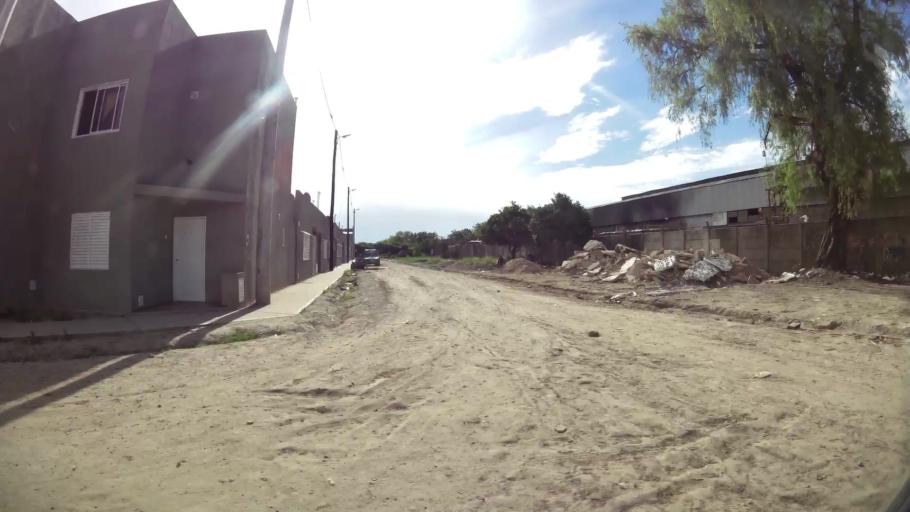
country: AR
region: Santa Fe
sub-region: Departamento de Rosario
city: Rosario
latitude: -32.9174
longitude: -60.6921
